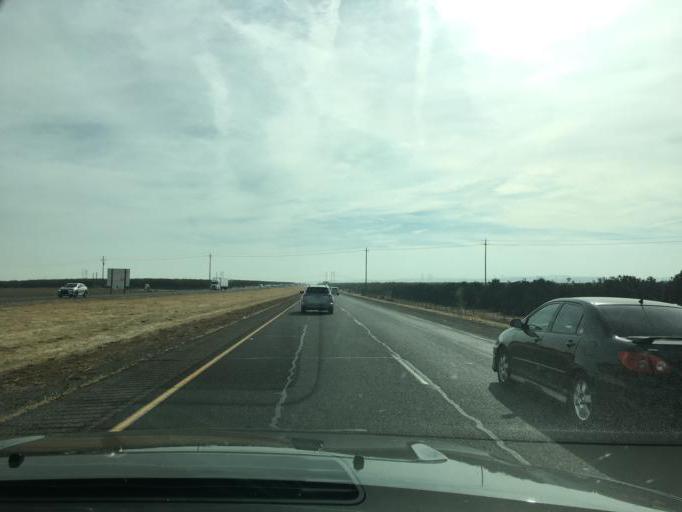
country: US
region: California
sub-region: Fresno County
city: Huron
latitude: 36.1249
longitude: -120.1474
